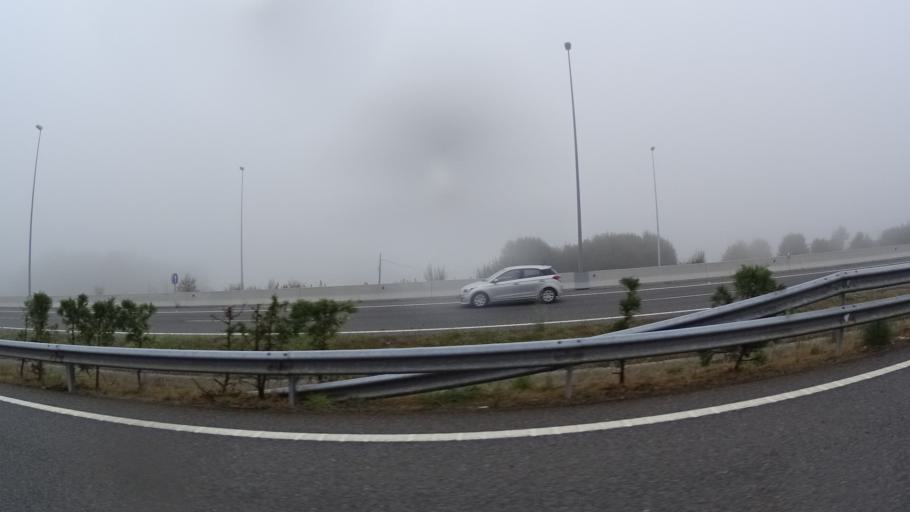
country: ES
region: Galicia
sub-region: Provincia de Lugo
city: Corgo
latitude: 42.9678
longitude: -7.4900
